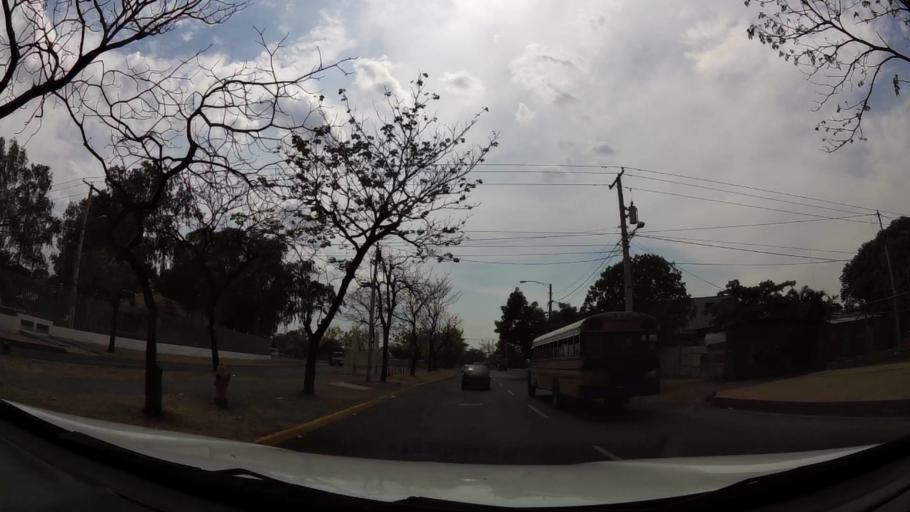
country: NI
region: Managua
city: Managua
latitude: 12.1511
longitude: -86.2750
